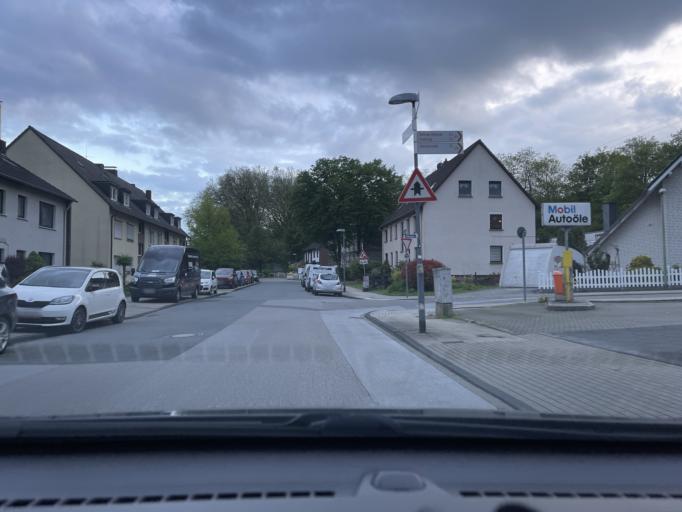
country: DE
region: North Rhine-Westphalia
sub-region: Regierungsbezirk Munster
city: Bottrop
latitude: 51.4780
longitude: 6.9466
